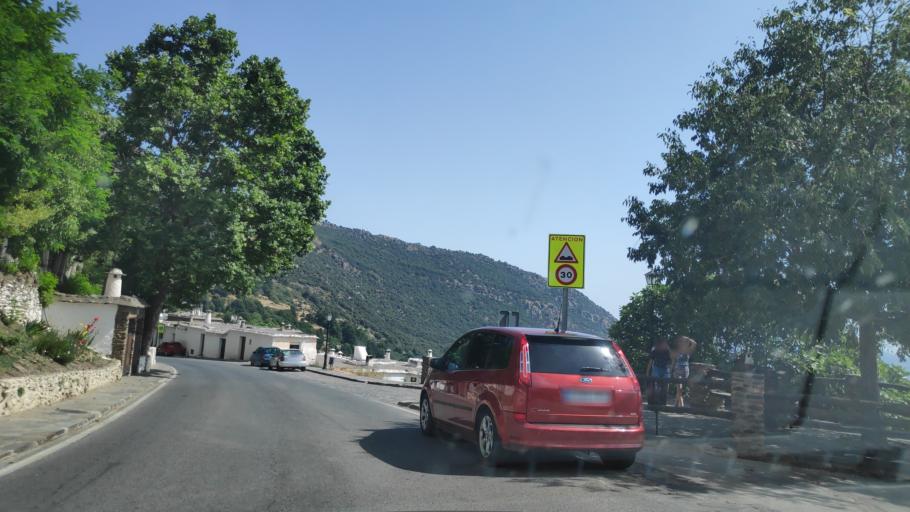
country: ES
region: Andalusia
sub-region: Provincia de Granada
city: Bubion
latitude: 36.9501
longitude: -3.3555
